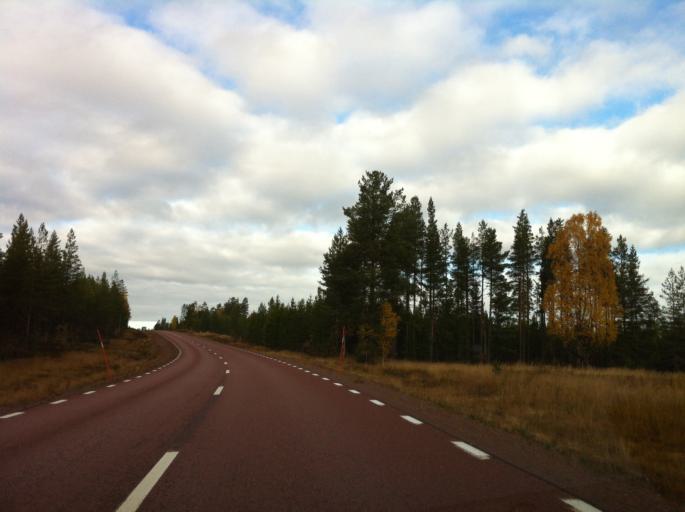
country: SE
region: Dalarna
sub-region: Alvdalens Kommun
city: AElvdalen
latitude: 61.5465
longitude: 13.3354
